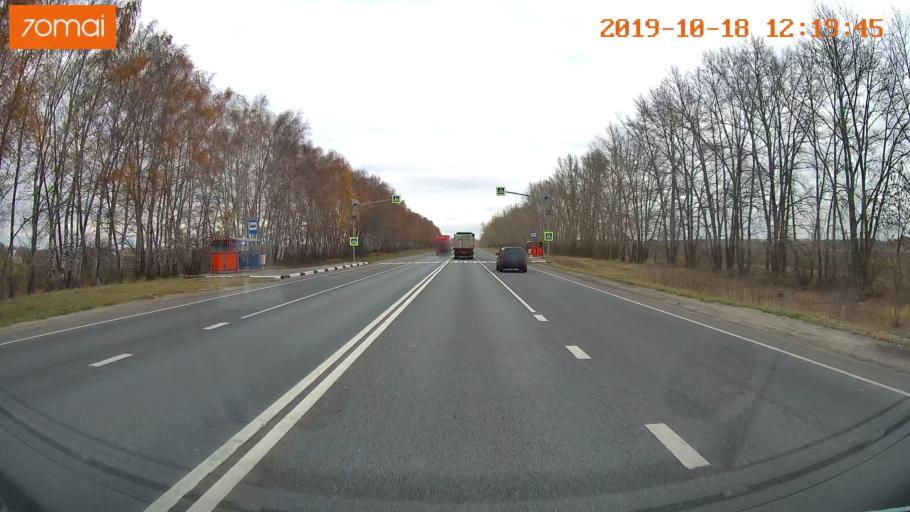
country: RU
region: Rjazan
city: Zakharovo
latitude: 54.4870
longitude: 39.4718
